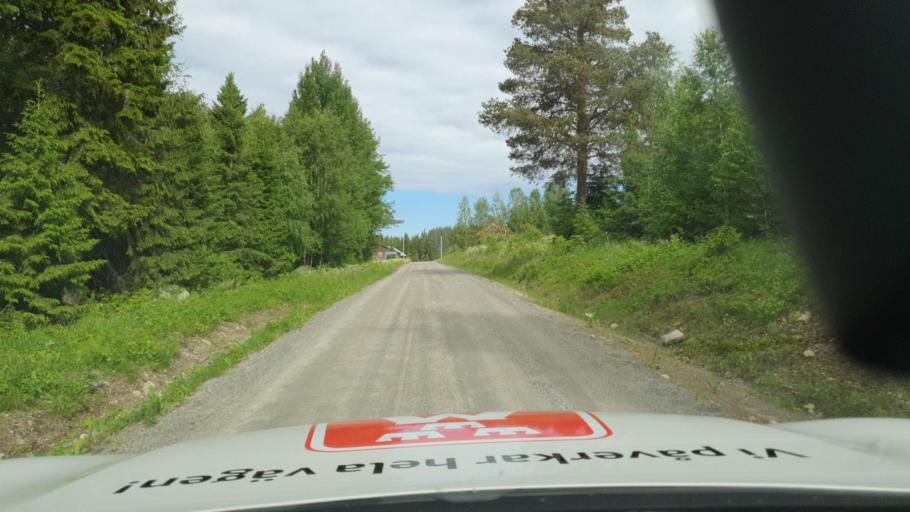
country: SE
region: Vaesterbotten
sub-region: Skelleftea Kommun
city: Langsele
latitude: 64.5920
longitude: 20.2951
